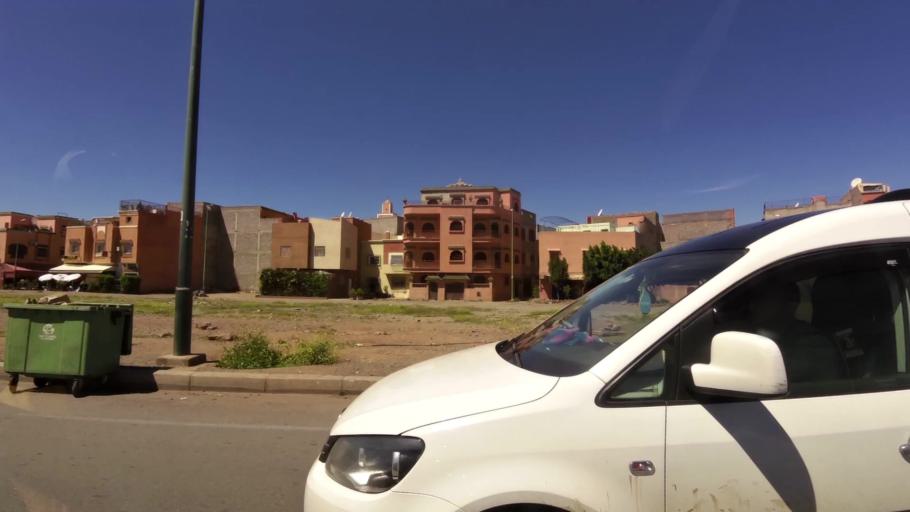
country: MA
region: Marrakech-Tensift-Al Haouz
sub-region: Marrakech
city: Marrakesh
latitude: 31.5747
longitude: -7.9813
